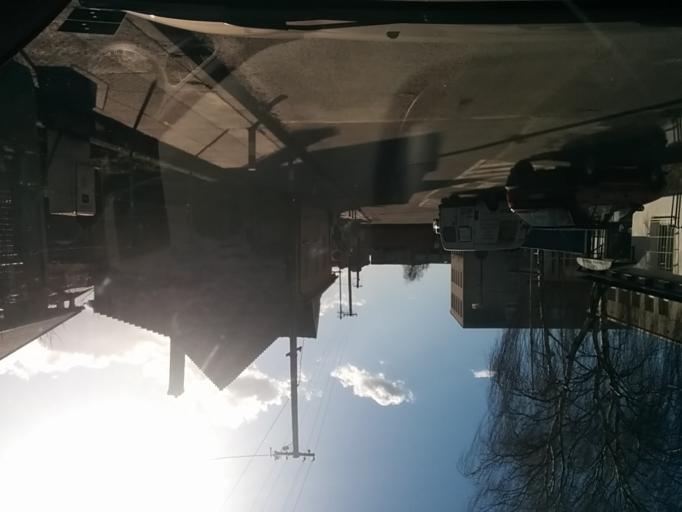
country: SK
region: Trenciansky
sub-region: Okres Nove Mesto nad Vahom
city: Nove Mesto nad Vahom
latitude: 48.7606
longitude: 17.8382
